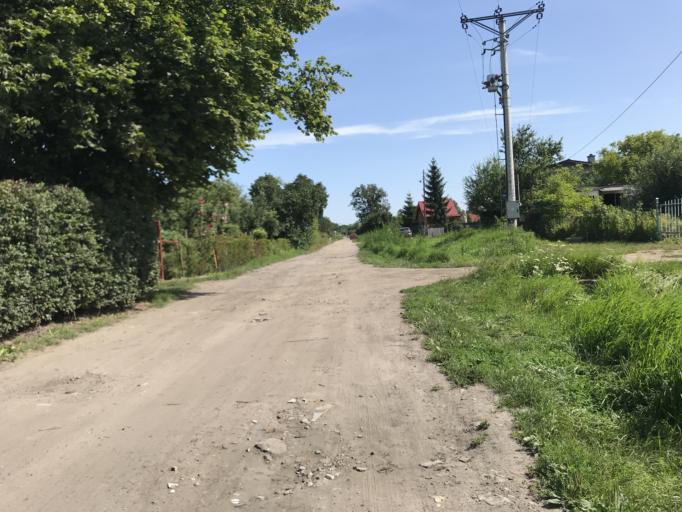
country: PL
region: Pomeranian Voivodeship
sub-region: Gdansk
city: Gdansk
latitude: 54.3399
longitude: 18.6735
